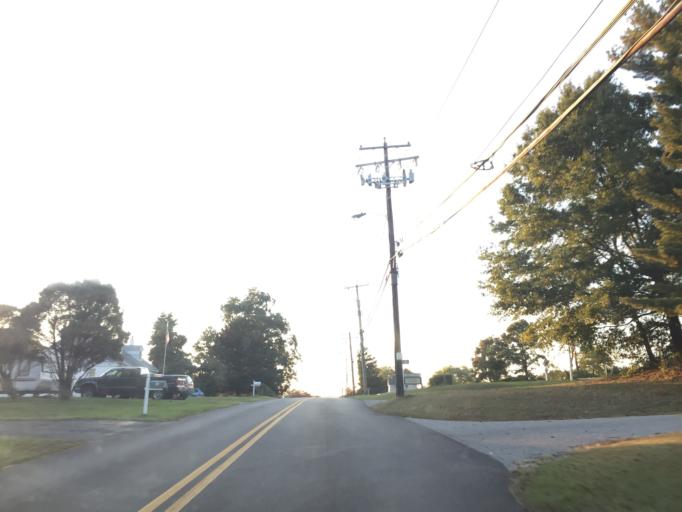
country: US
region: Maryland
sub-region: Baltimore County
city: Essex
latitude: 39.3180
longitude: -76.4623
